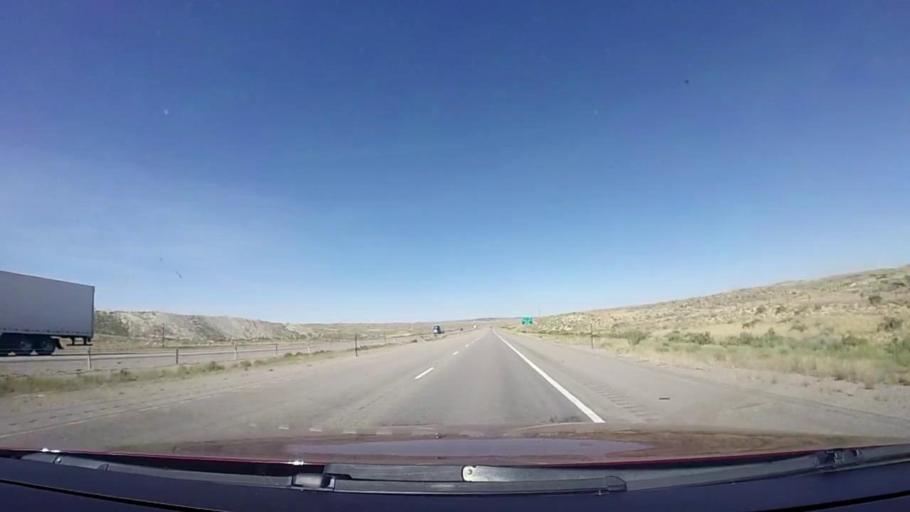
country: US
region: Wyoming
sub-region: Sweetwater County
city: Rock Springs
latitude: 41.6471
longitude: -108.6650
